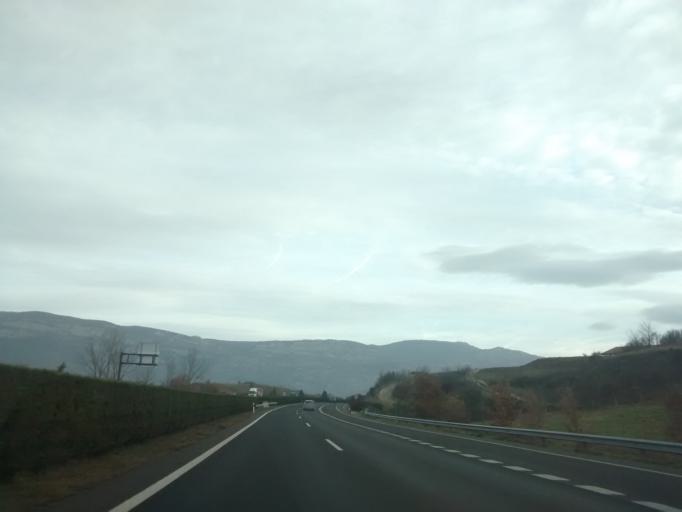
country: ES
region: Navarre
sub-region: Provincia de Navarra
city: Arbizu
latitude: 42.9113
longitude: -2.0366
